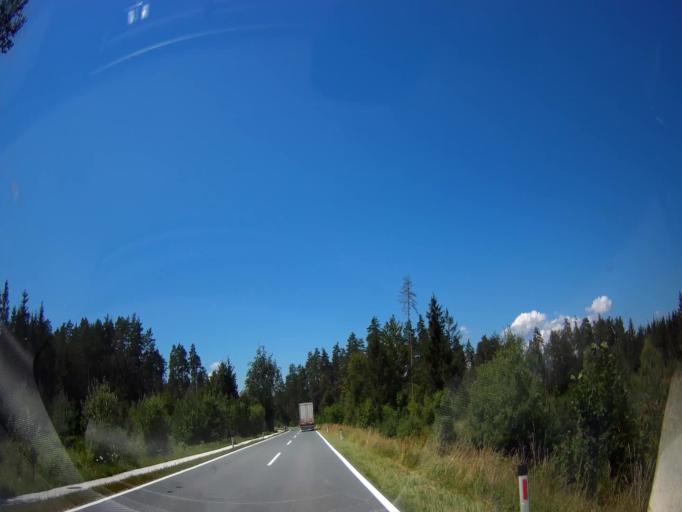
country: AT
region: Carinthia
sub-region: Politischer Bezirk Volkermarkt
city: Eberndorf
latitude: 46.6179
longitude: 14.6569
